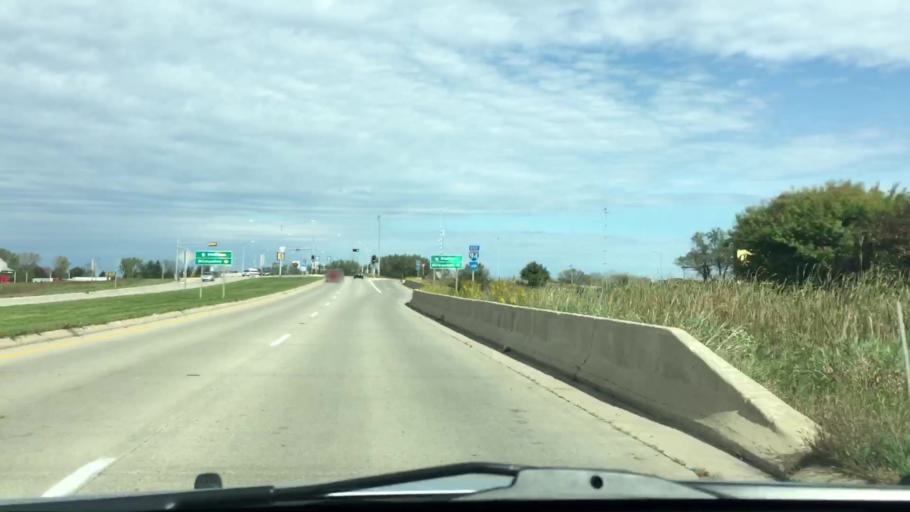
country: US
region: Wisconsin
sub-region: Waukesha County
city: Pewaukee
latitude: 43.0444
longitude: -88.2555
